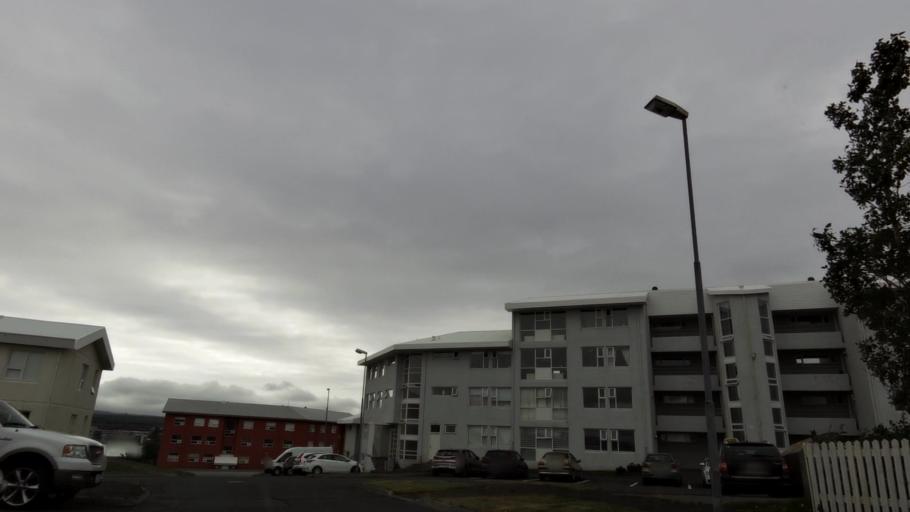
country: IS
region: Capital Region
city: Hafnarfjoerdur
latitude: 64.0563
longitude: -21.9807
